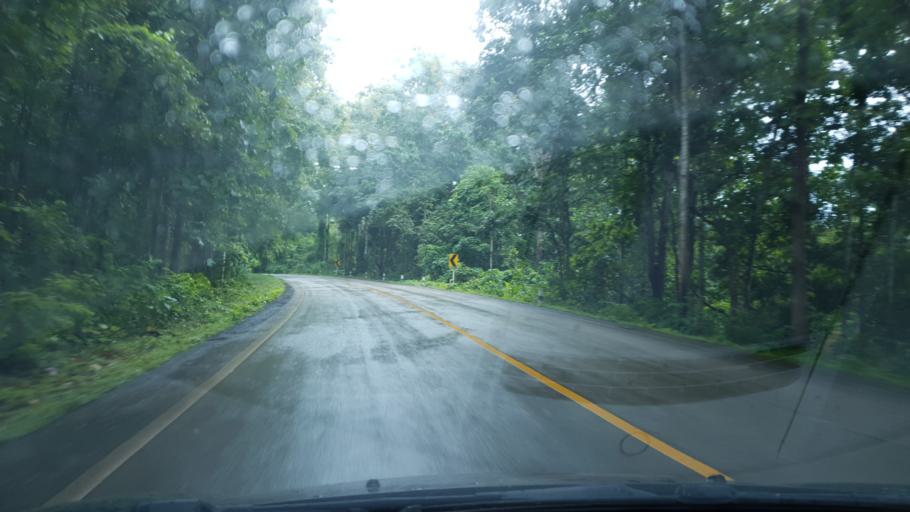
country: TH
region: Mae Hong Son
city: Pa Pae
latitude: 18.2532
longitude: 97.9423
